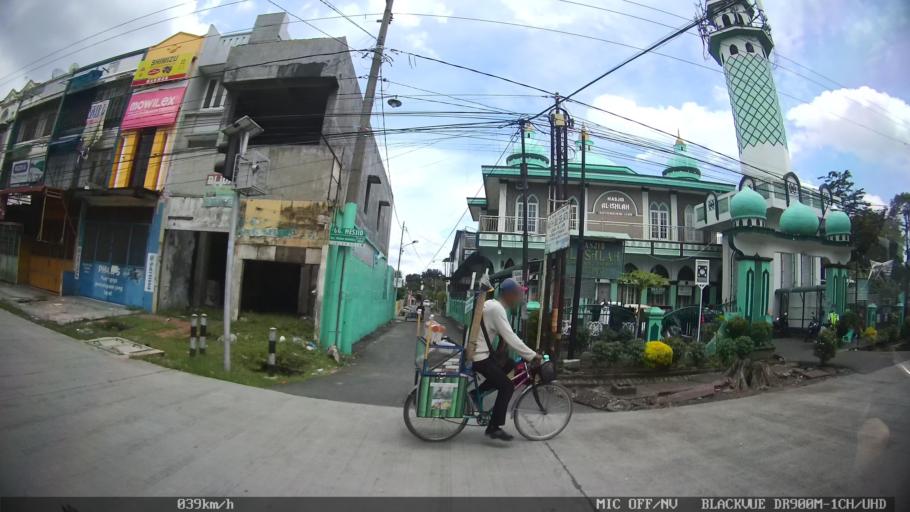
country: ID
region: North Sumatra
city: Medan
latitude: 3.5947
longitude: 98.6446
